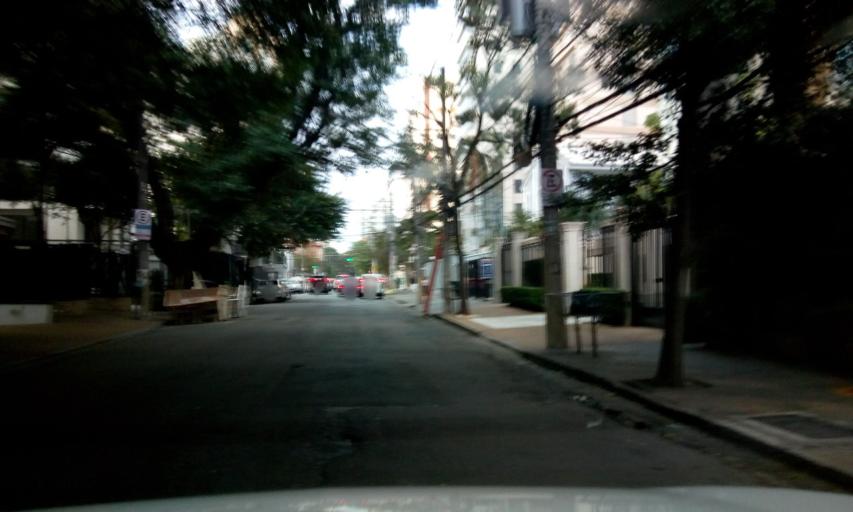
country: BR
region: Sao Paulo
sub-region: Sao Paulo
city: Sao Paulo
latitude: -23.5818
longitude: -46.6783
